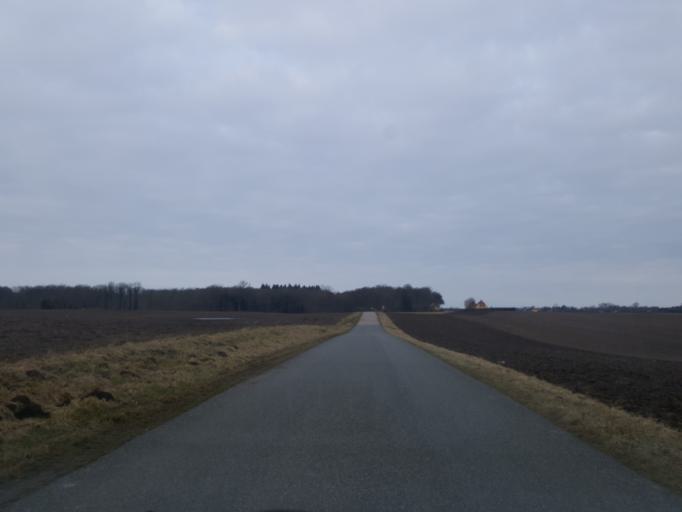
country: DK
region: Zealand
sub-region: Vordingborg Kommune
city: Neder Vindinge
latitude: 55.0303
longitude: 11.8509
